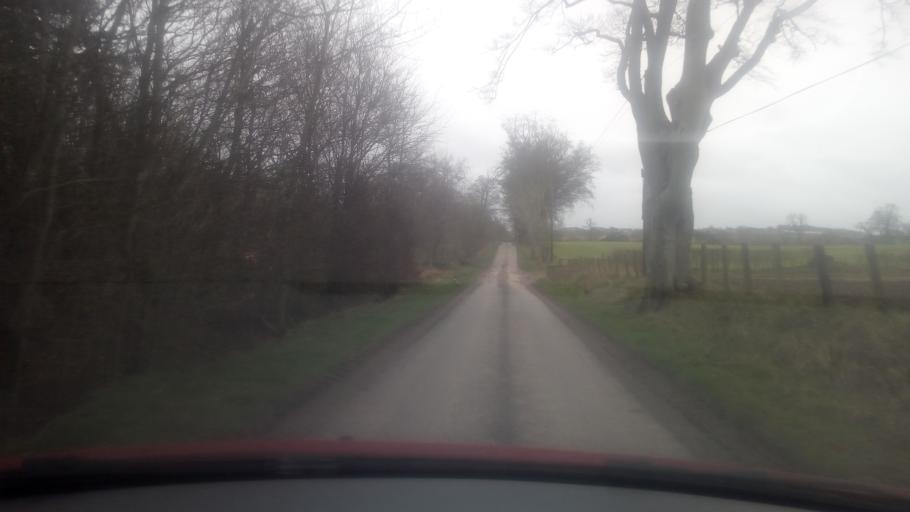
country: GB
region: Scotland
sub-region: The Scottish Borders
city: Jedburgh
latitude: 55.4231
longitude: -2.6429
